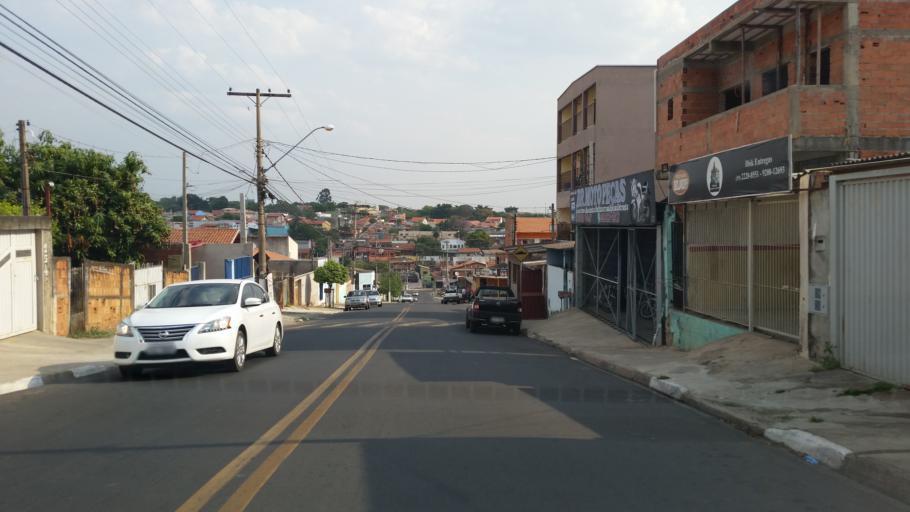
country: BR
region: Sao Paulo
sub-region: Hortolandia
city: Hortolandia
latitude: -22.8839
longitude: -47.1772
